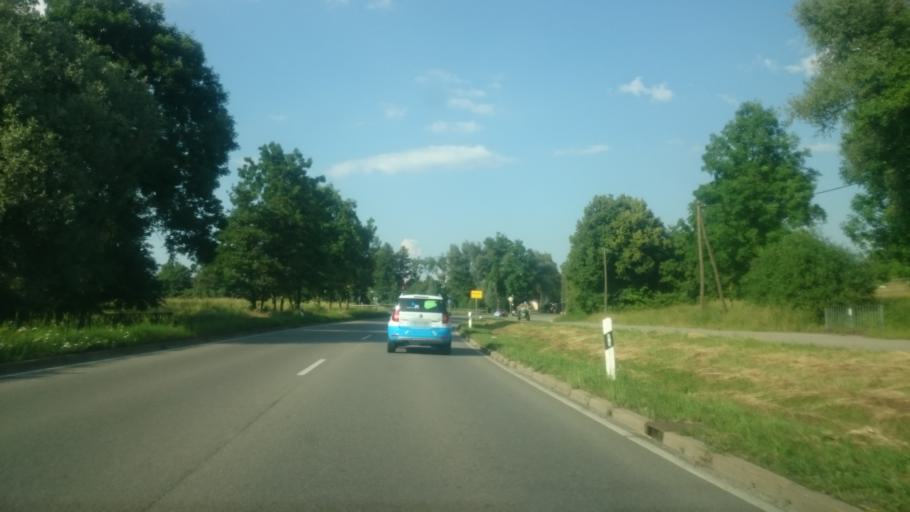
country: DE
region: Baden-Wuerttemberg
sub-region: Tuebingen Region
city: Gomaringen
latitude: 48.4497
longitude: 9.0801
